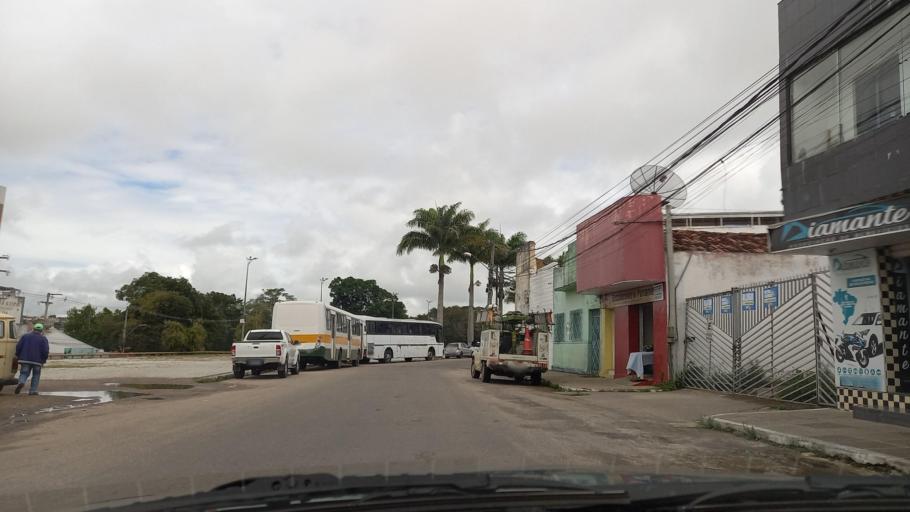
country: BR
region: Pernambuco
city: Garanhuns
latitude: -8.8873
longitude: -36.4912
